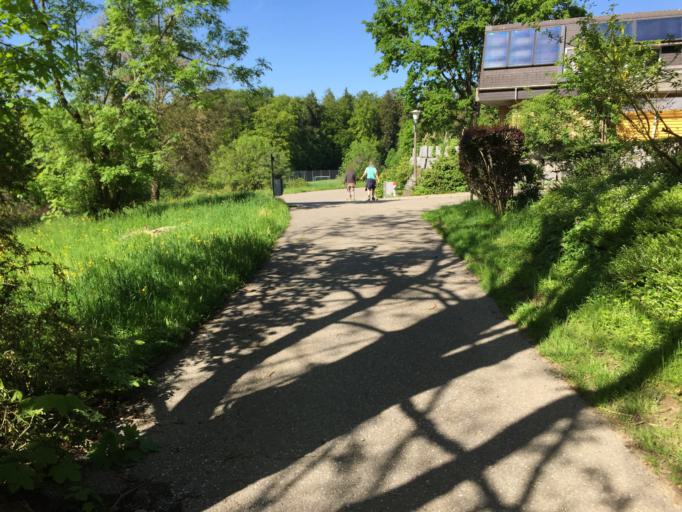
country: CH
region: Zurich
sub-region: Bezirk Uster
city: Pfaffhausen
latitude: 47.3665
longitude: 8.6197
